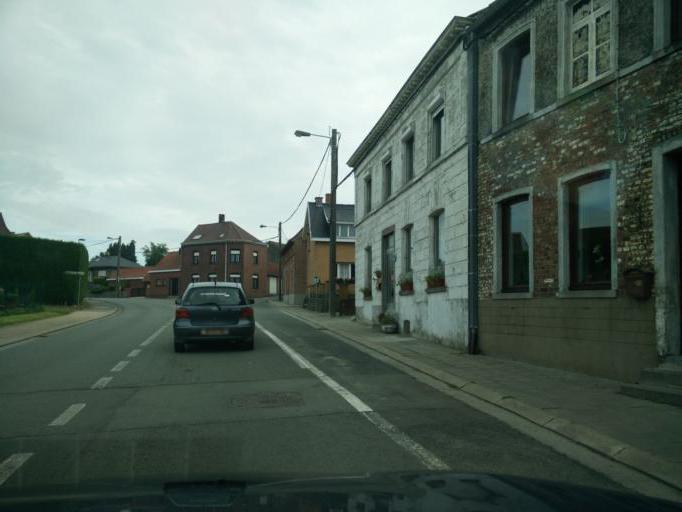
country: BE
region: Wallonia
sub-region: Province du Hainaut
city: Flobecq
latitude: 50.7400
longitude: 3.7375
